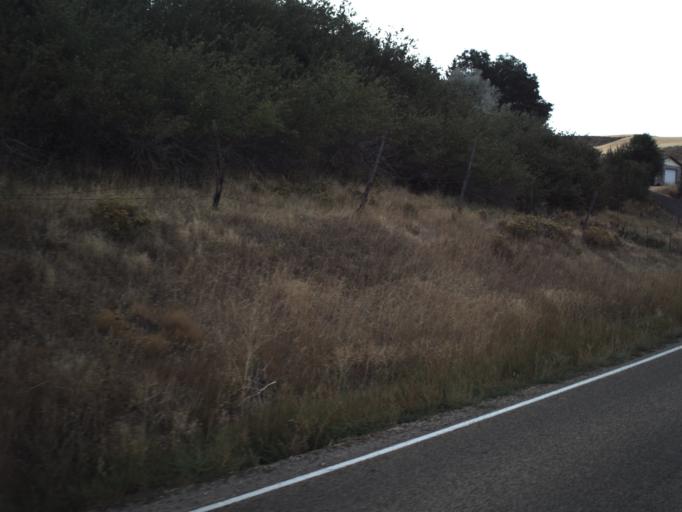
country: US
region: Utah
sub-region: Morgan County
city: Morgan
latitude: 41.0100
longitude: -111.6771
